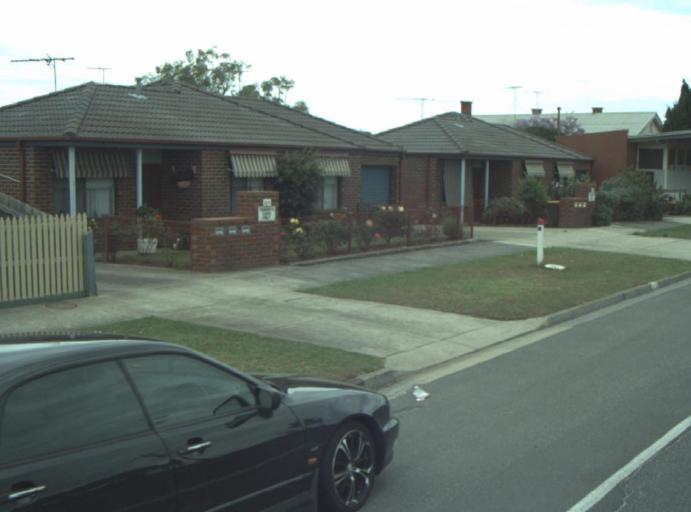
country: AU
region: Victoria
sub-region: Greater Geelong
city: Breakwater
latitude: -38.1728
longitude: 144.3838
